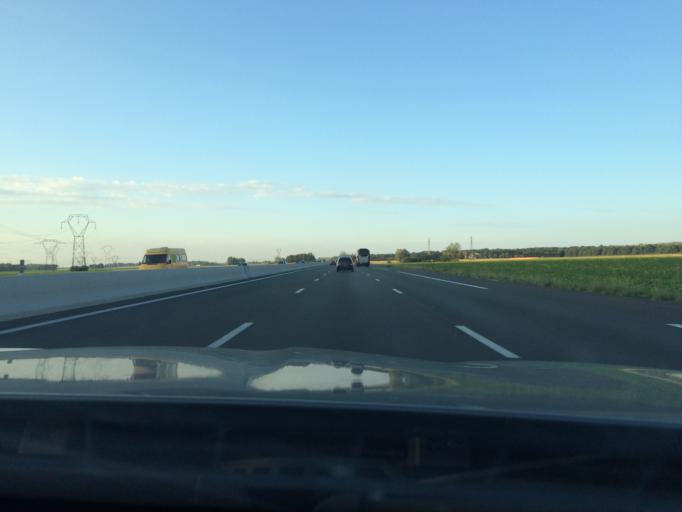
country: FR
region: Ile-de-France
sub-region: Departement de l'Essonne
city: Le Coudray-Montceaux
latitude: 48.5341
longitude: 2.5005
